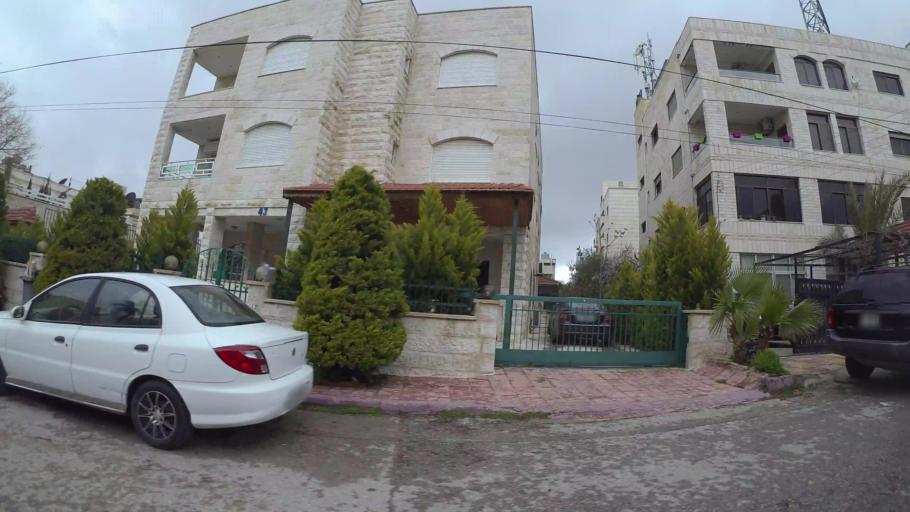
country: JO
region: Amman
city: Wadi as Sir
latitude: 31.9538
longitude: 35.8600
